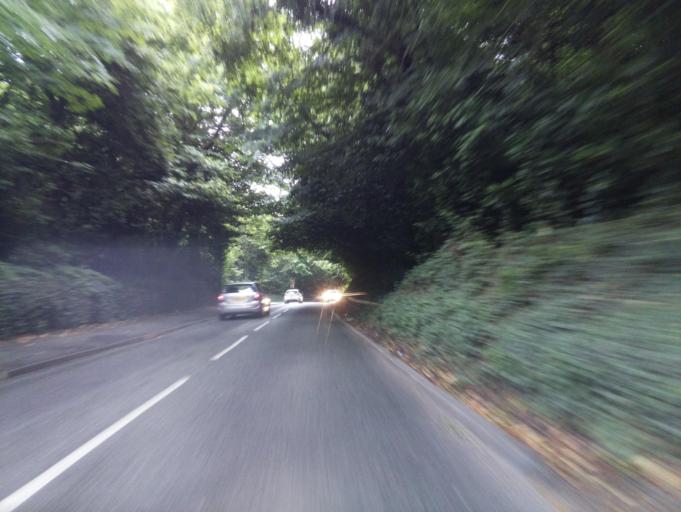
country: GB
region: England
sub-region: Surrey
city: Redhill
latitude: 51.2354
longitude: -0.1767
